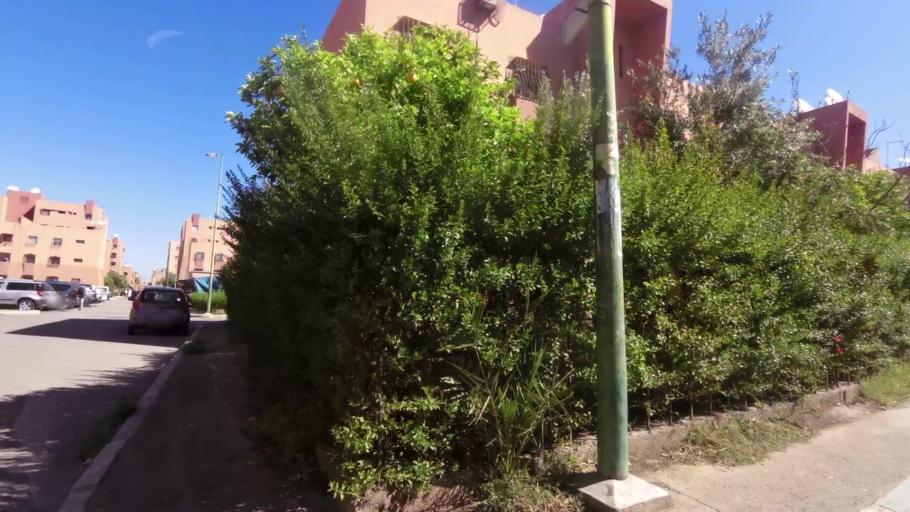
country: MA
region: Marrakech-Tensift-Al Haouz
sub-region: Marrakech
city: Marrakesh
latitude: 31.5907
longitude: -8.0472
